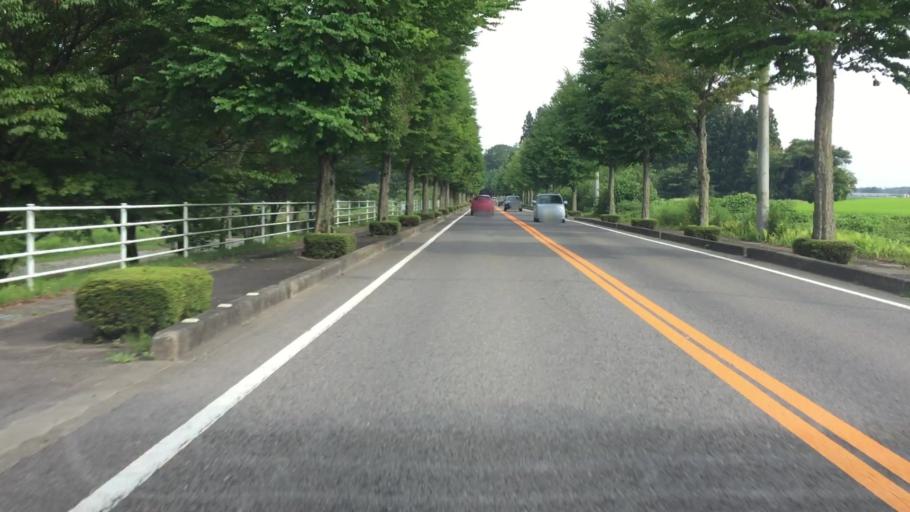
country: JP
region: Tochigi
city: Kuroiso
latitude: 36.9831
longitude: 139.9600
